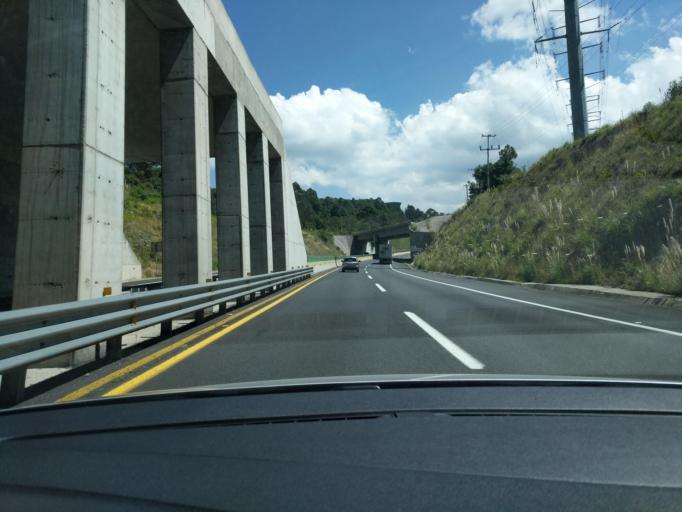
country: MX
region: Morelos
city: San Jeronimo Acazulco
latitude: 19.2969
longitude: -99.4121
